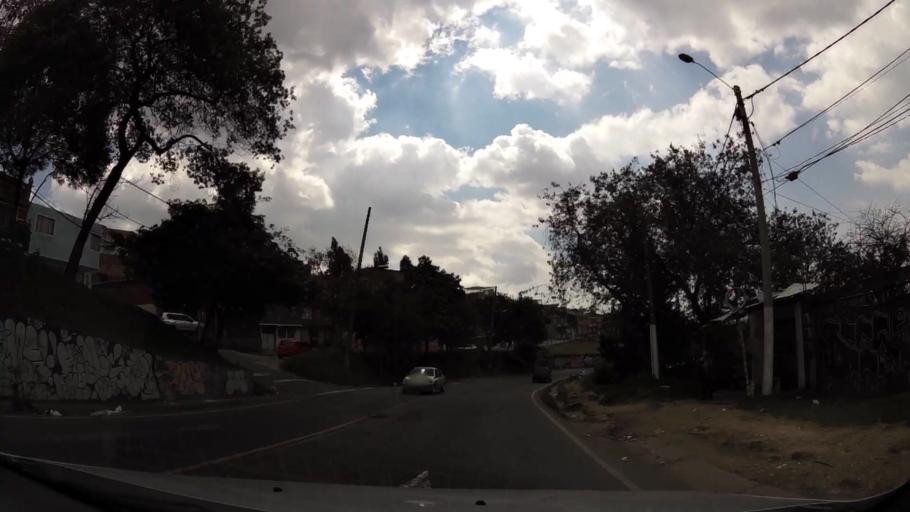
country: CO
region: Bogota D.C.
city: Bogota
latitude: 4.5558
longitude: -74.0948
